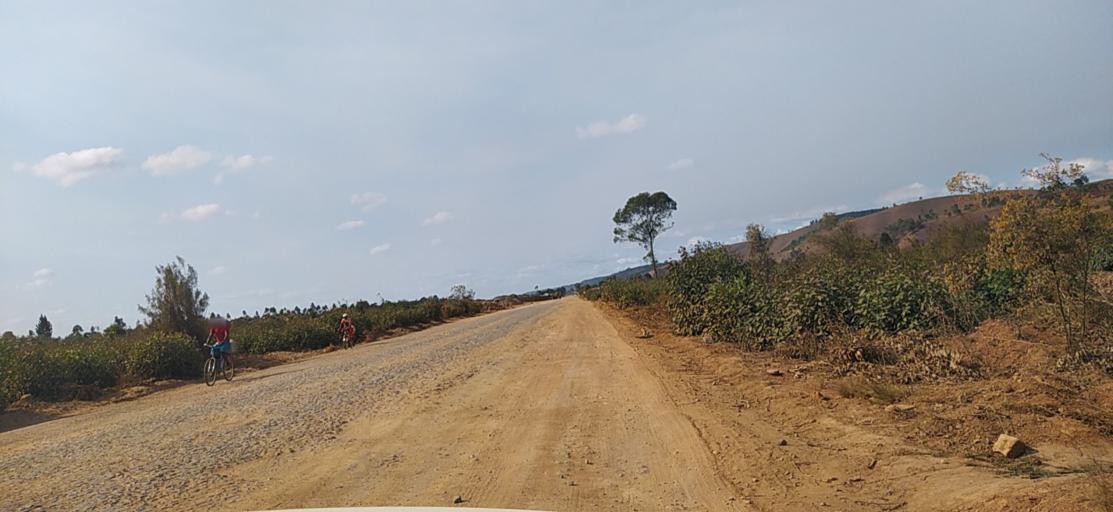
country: MG
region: Alaotra Mangoro
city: Moramanga
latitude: -18.6785
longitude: 48.2726
